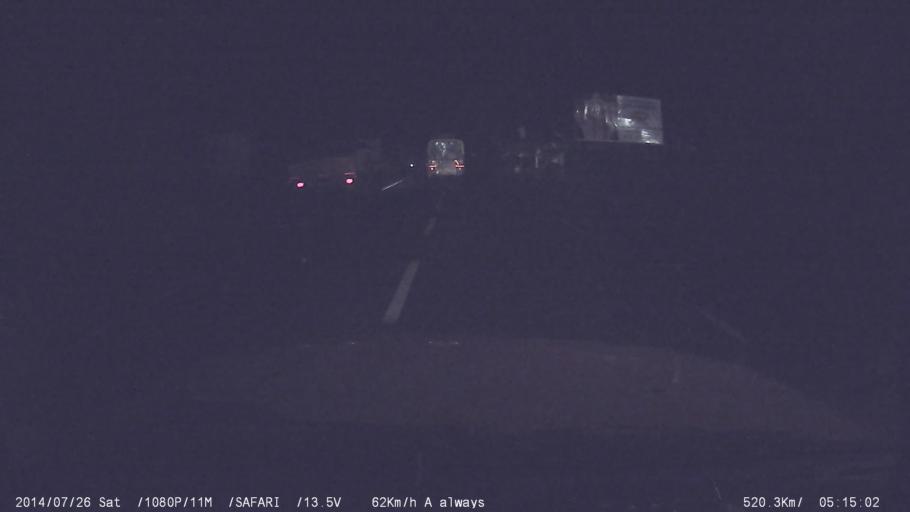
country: IN
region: Kerala
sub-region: Ernakulam
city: Muvattupula
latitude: 10.0277
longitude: 76.5517
